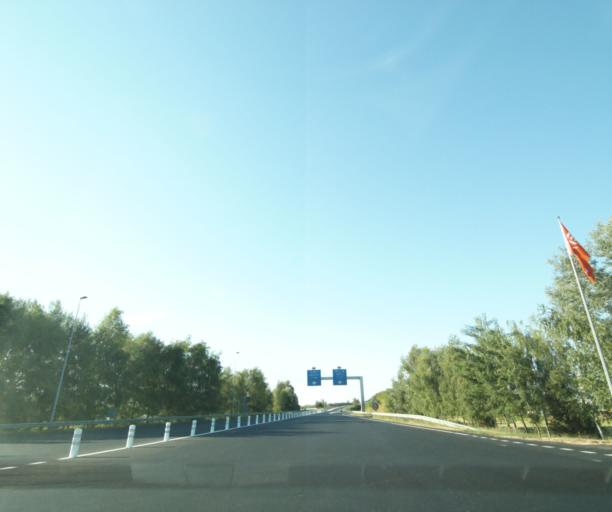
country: FR
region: Ile-de-France
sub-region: Departement de Seine-et-Marne
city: Marolles-sur-Seine
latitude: 48.3798
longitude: 3.0204
